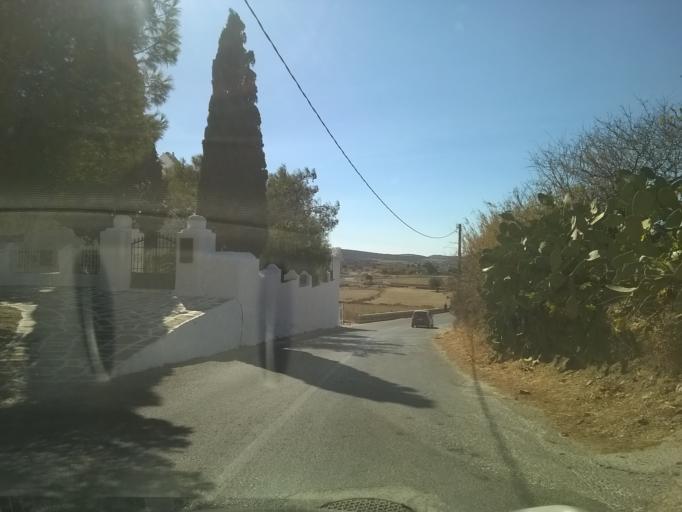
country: GR
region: South Aegean
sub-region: Nomos Kykladon
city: Filotion
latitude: 37.0465
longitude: 25.4332
